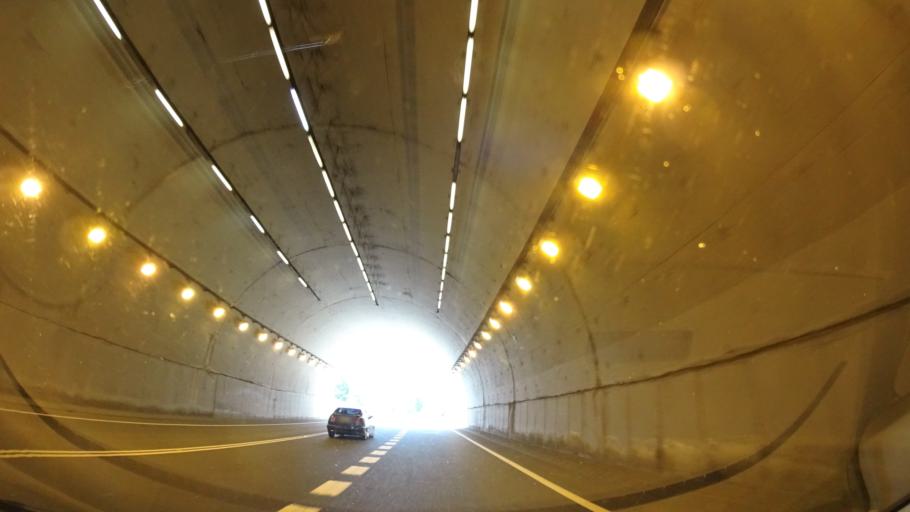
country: ES
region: Basque Country
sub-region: Bizkaia
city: Zeanuri
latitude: 43.0992
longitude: -2.7523
